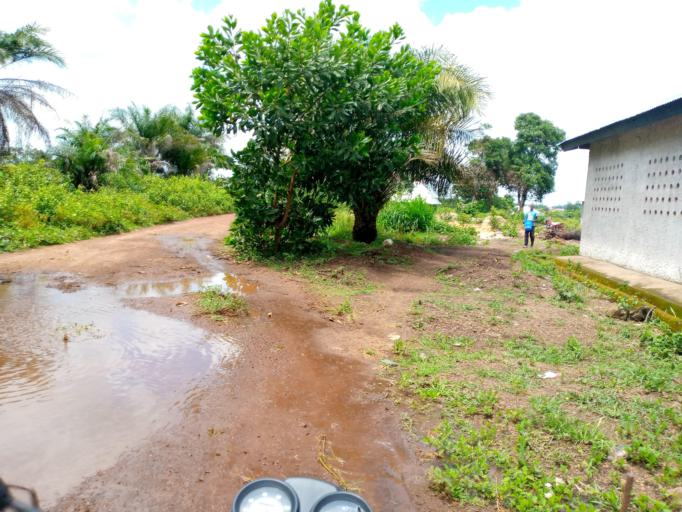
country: SL
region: Northern Province
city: Magburaka
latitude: 8.7255
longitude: -11.9234
